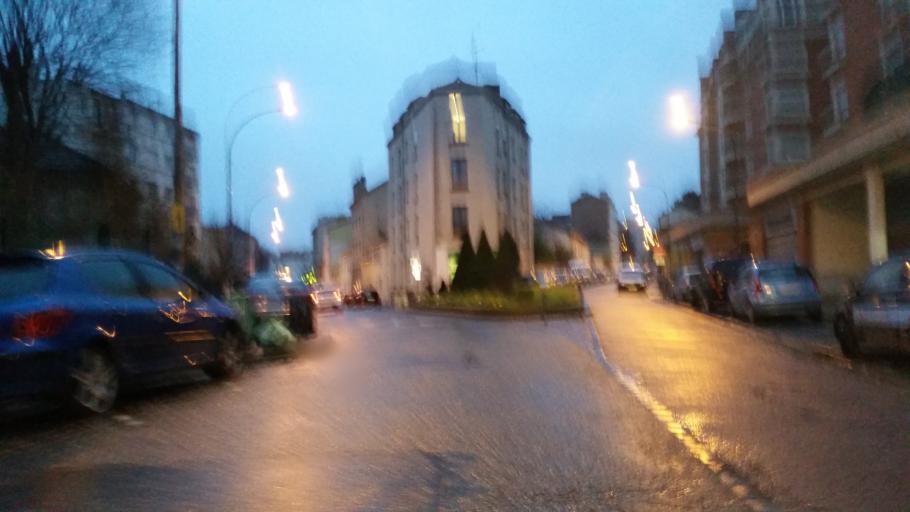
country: FR
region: Ile-de-France
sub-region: Departement du Val-de-Marne
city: Ivry-sur-Seine
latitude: 48.8079
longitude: 2.3886
